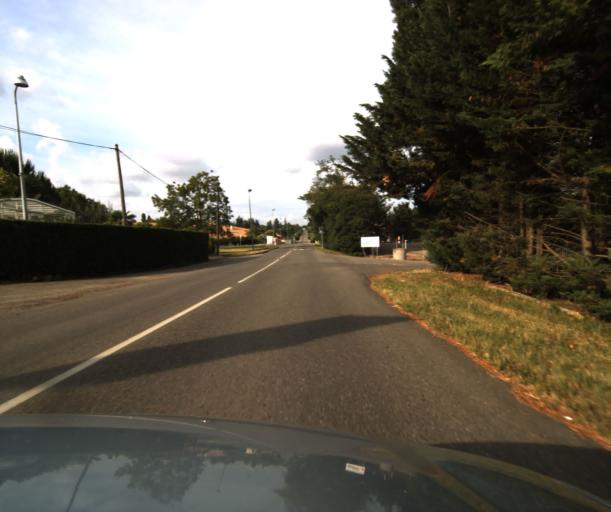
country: FR
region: Midi-Pyrenees
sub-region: Departement du Tarn-et-Garonne
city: Beaumont-de-Lomagne
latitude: 43.8758
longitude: 0.9765
